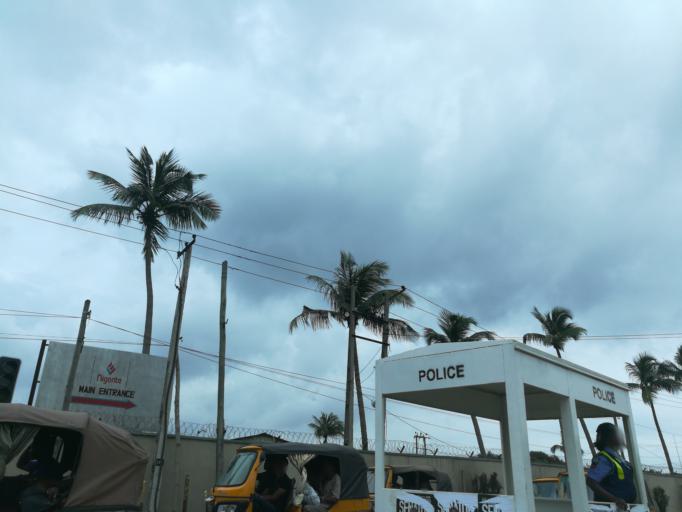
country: NG
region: Lagos
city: Ikeja
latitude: 6.6048
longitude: 3.3371
